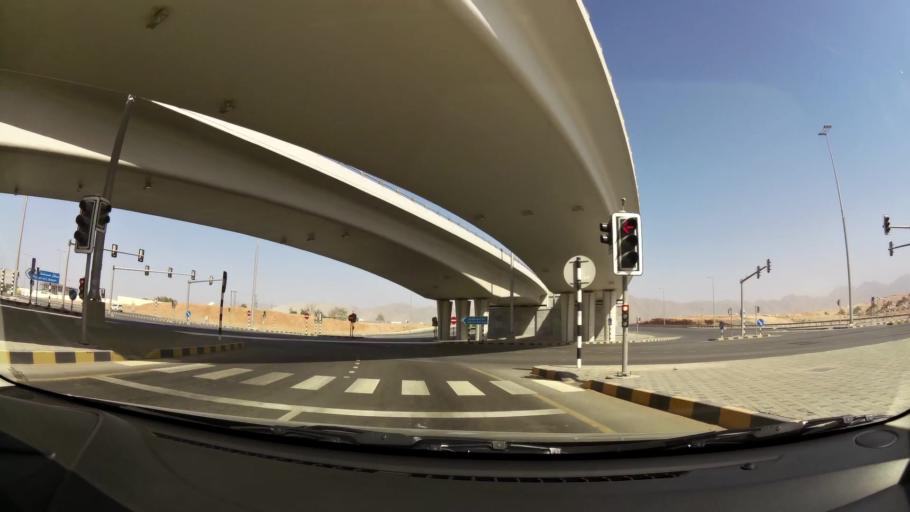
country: OM
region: Muhafazat Masqat
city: Bawshar
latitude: 23.5702
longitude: 58.3332
